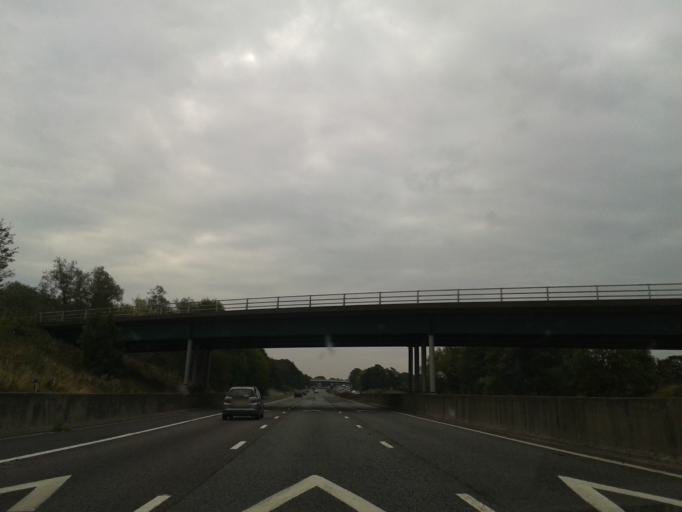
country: GB
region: England
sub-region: Lancashire
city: Catterall
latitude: 53.8527
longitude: -2.7330
